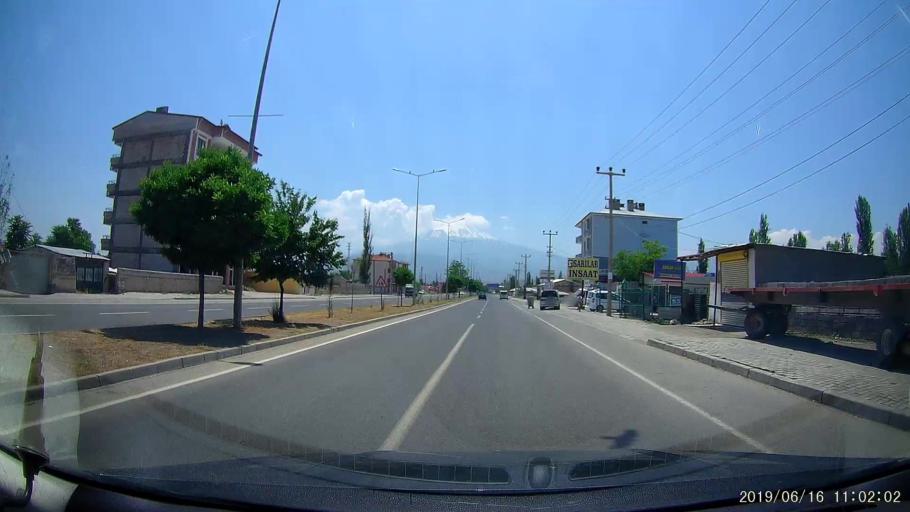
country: TR
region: Igdir
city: Igdir
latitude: 39.9104
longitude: 44.0558
